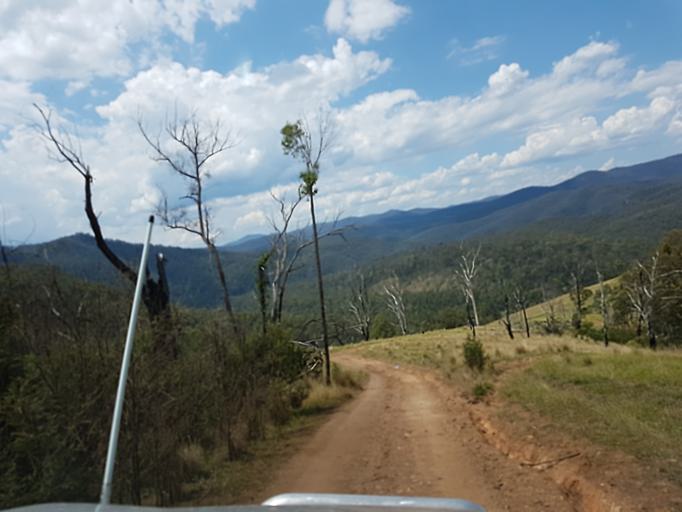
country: AU
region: Victoria
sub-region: East Gippsland
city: Lakes Entrance
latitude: -37.3975
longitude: 148.3233
